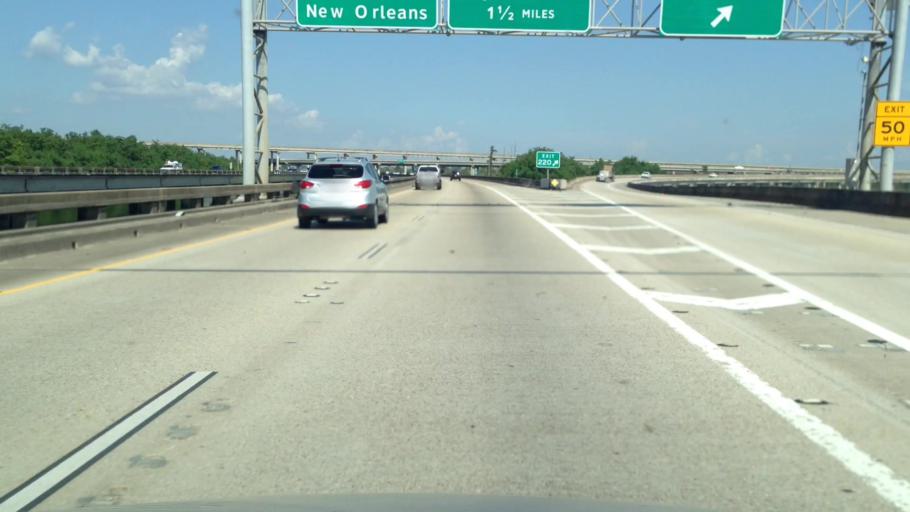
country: US
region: Louisiana
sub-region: Saint Charles Parish
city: Ama
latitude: 30.0078
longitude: -90.2984
